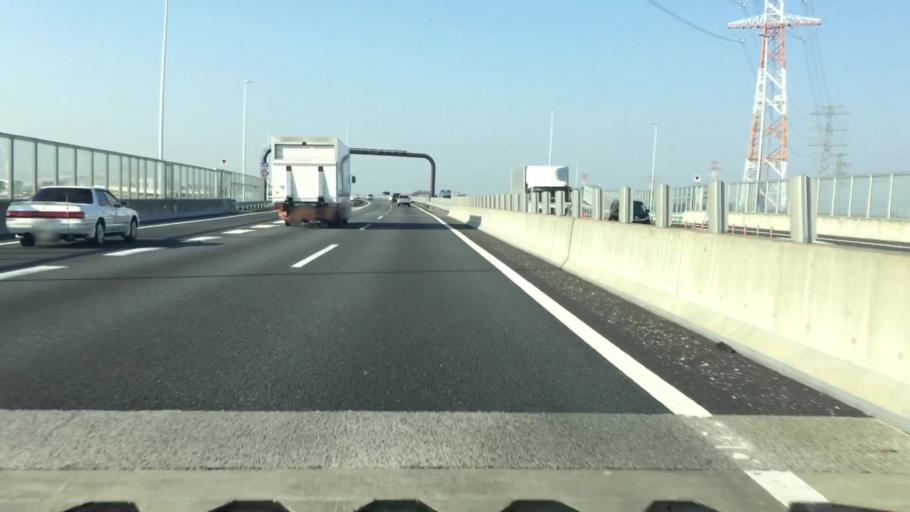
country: JP
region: Saitama
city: Okegawa
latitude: 36.0045
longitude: 139.5230
